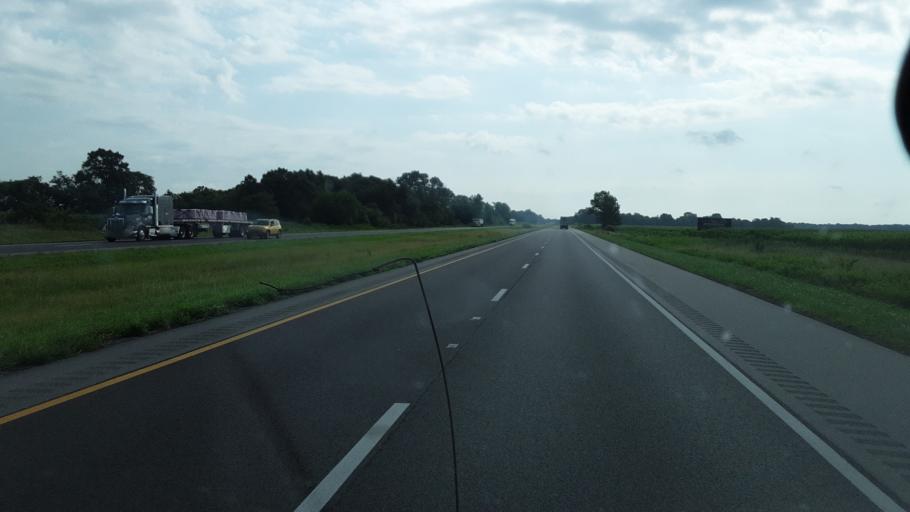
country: US
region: Illinois
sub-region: Bond County
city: Greenville
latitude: 38.8557
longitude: -89.4345
